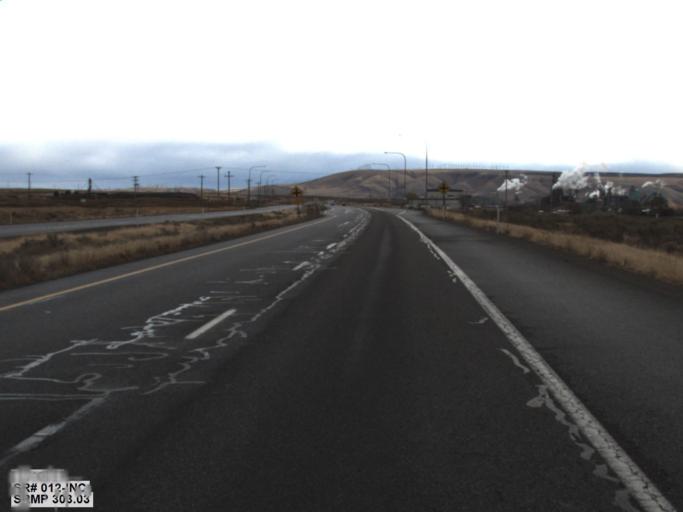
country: US
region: Washington
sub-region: Benton County
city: Finley
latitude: 46.1192
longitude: -118.9269
